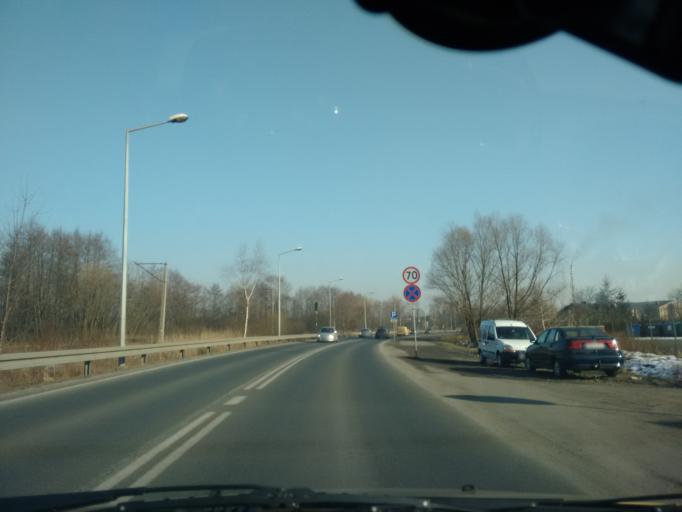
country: PL
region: Lesser Poland Voivodeship
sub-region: Powiat wadowicki
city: Wadowice
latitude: 49.8902
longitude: 19.4935
